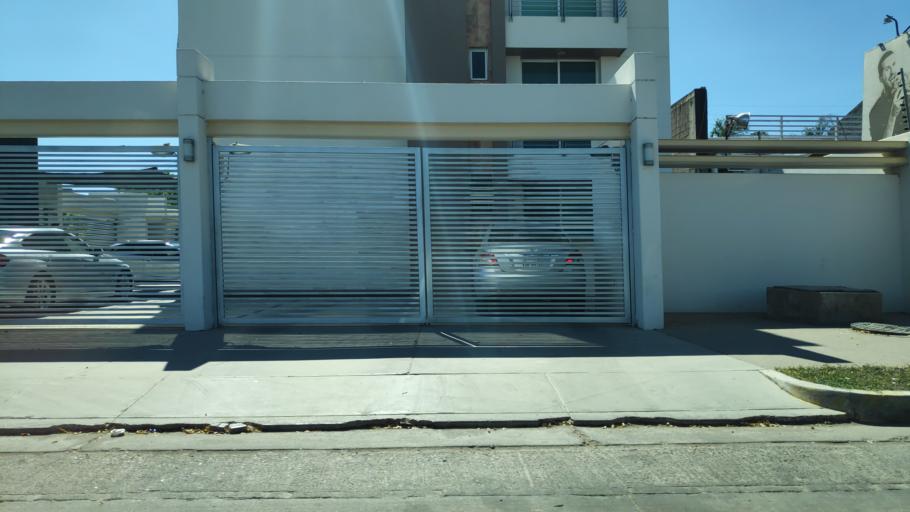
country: MX
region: Sinaloa
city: Culiacan
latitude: 24.8281
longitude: -107.3999
